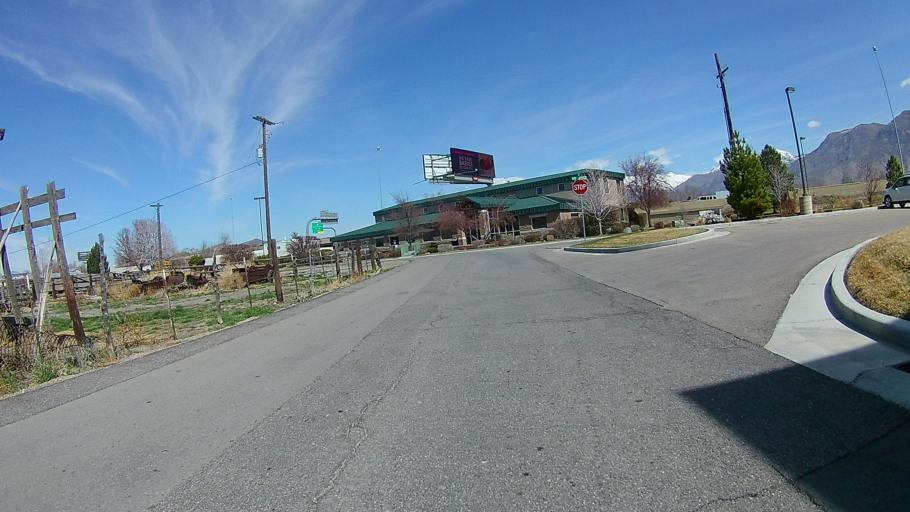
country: US
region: Utah
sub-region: Utah County
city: American Fork
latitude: 40.3641
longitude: -111.7932
